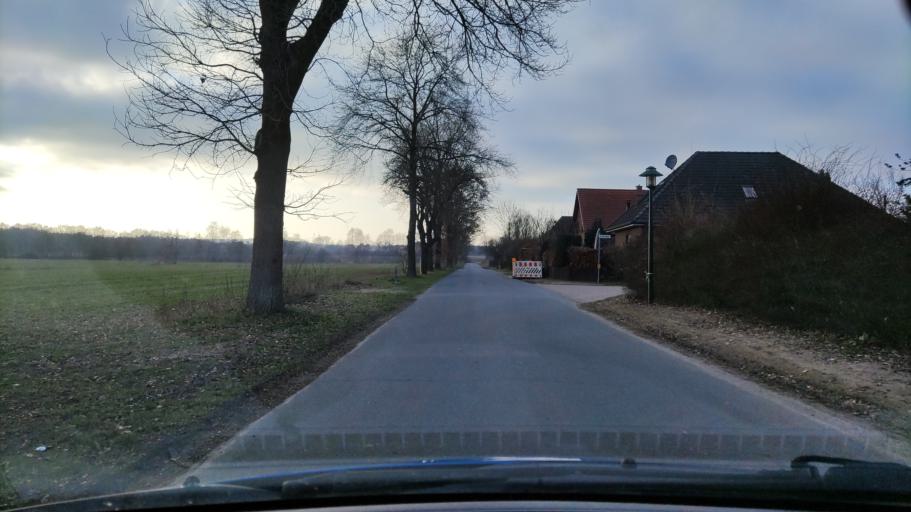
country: DE
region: Lower Saxony
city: Gerdau
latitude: 52.9681
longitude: 10.4156
